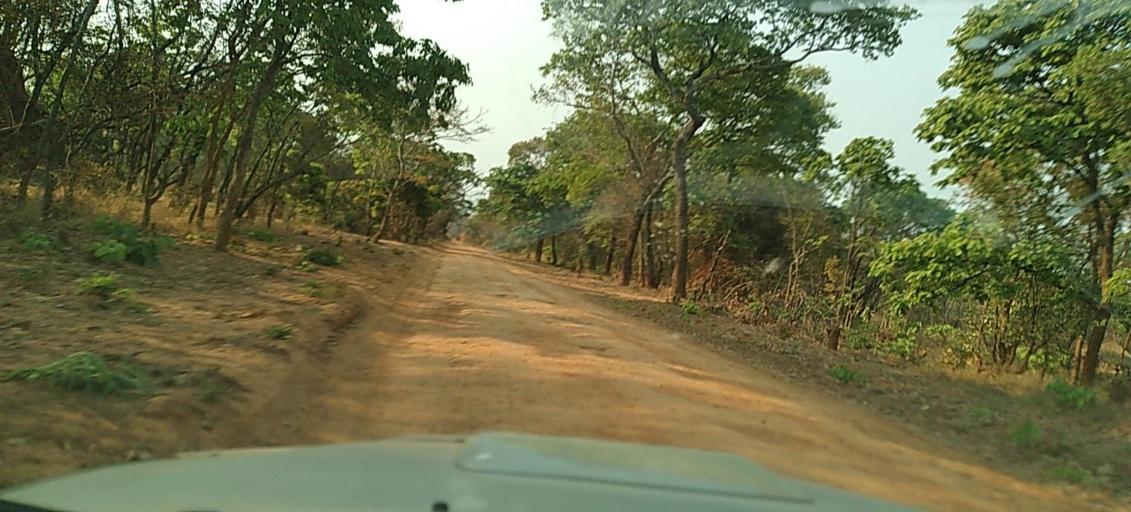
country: ZM
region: North-Western
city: Kasempa
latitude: -13.2886
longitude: 26.5551
